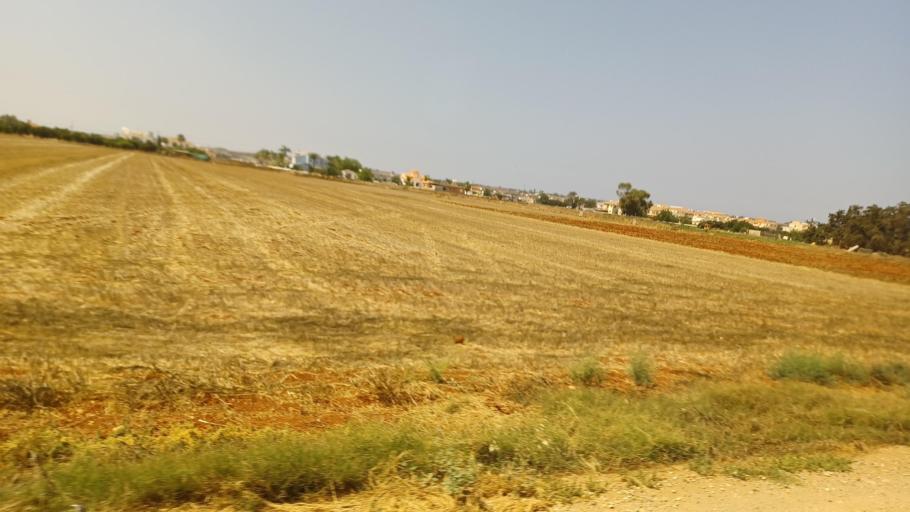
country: CY
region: Ammochostos
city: Liopetri
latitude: 34.9787
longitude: 33.8639
